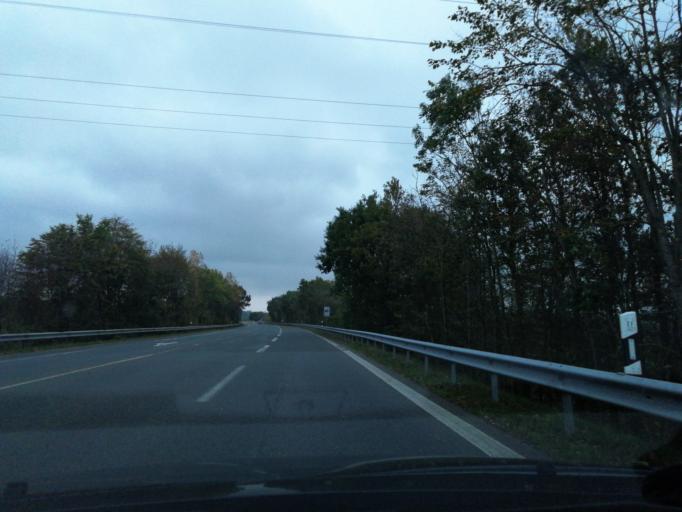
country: DE
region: Lower Saxony
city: Fedderwarden
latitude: 53.5443
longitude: 8.0501
